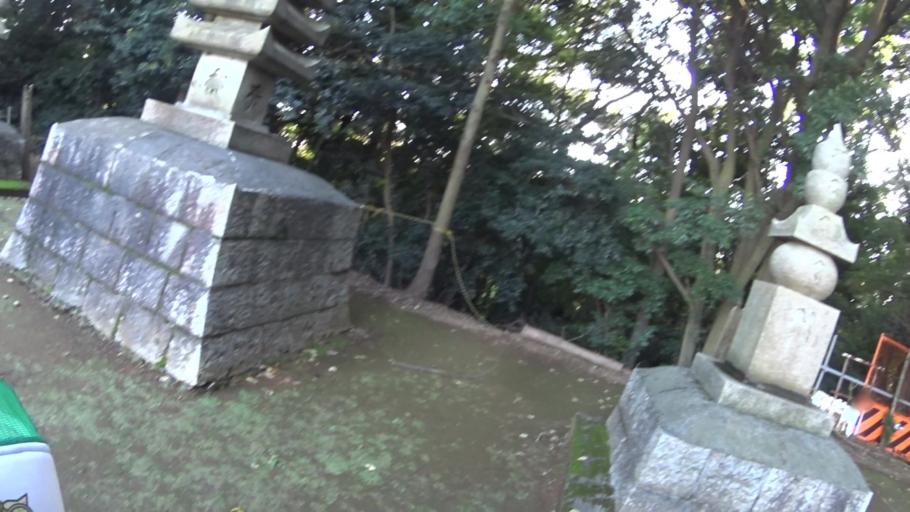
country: JP
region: Tokyo
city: Chofugaoka
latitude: 35.6305
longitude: 139.5122
